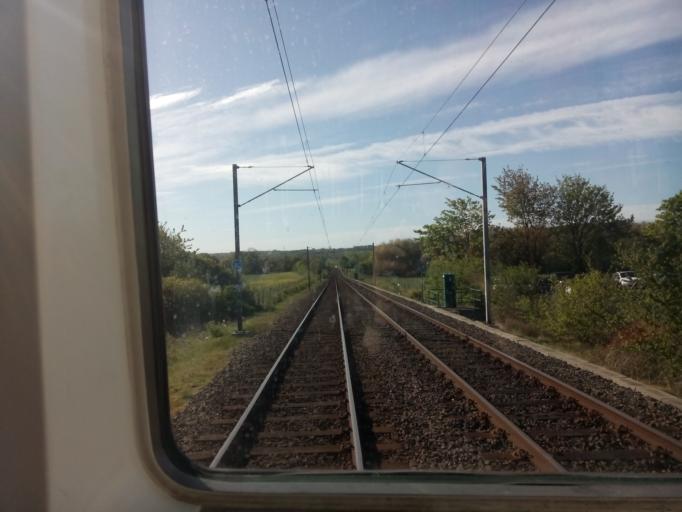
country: GB
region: England
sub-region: Newcastle upon Tyne
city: Dinnington
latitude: 55.0274
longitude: -1.7032
